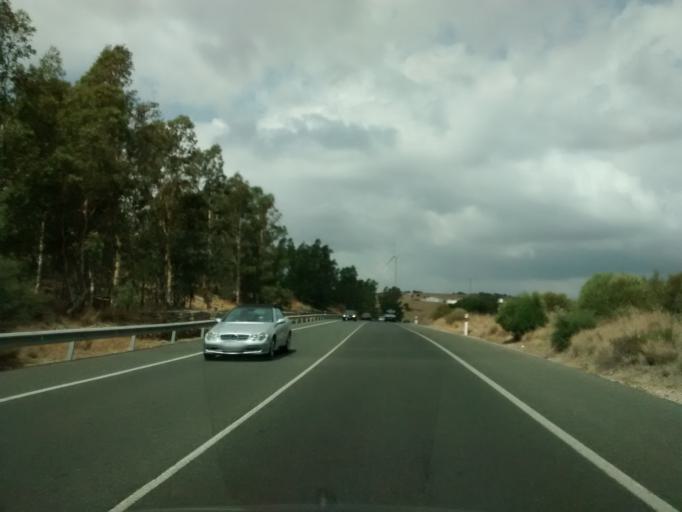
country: ES
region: Andalusia
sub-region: Provincia de Cadiz
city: Zahara de los Atunes
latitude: 36.1220
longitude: -5.7075
